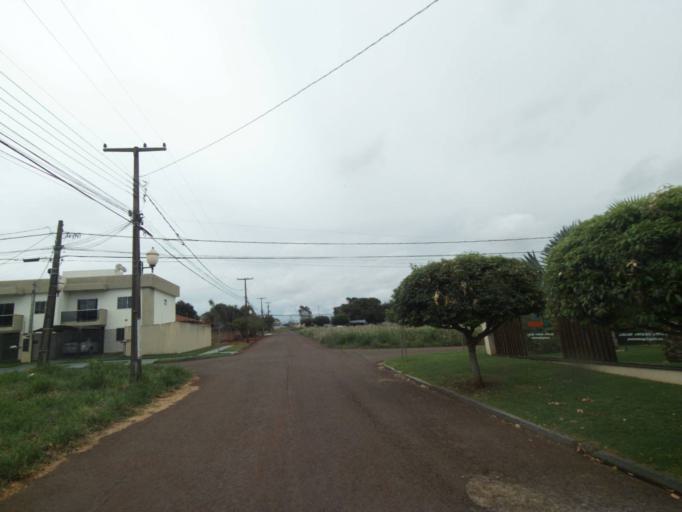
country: BR
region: Parana
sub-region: Campo Mourao
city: Campo Mourao
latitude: -24.0335
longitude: -52.3623
